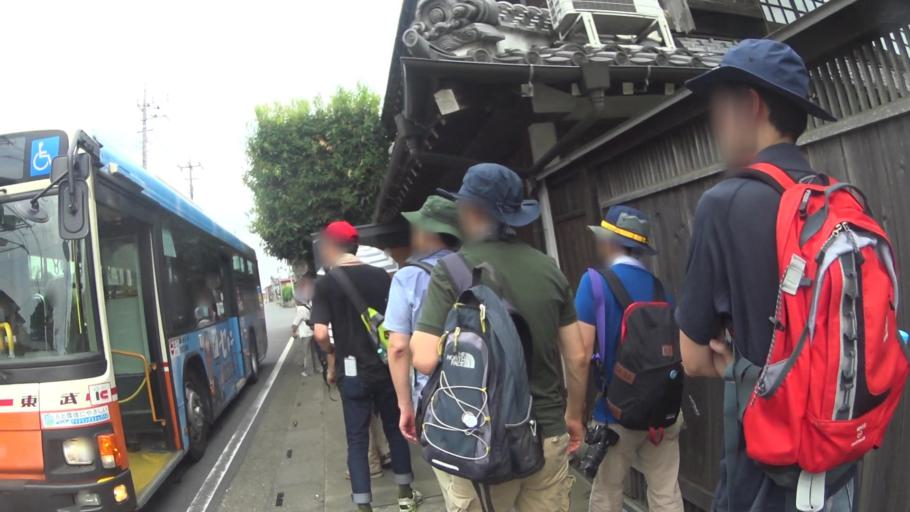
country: JP
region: Saitama
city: Okegawa
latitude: 35.9447
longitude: 139.5502
